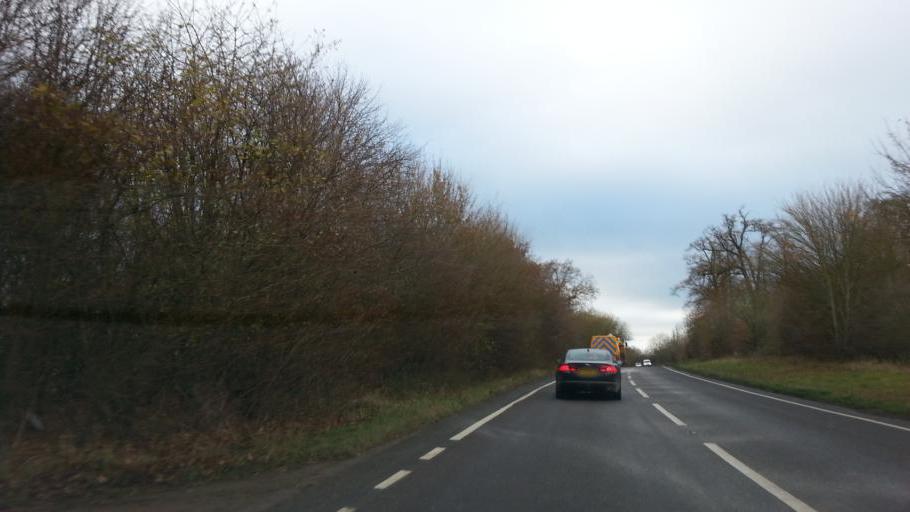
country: GB
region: England
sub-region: Norfolk
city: Diss
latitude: 52.3528
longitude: 1.0796
